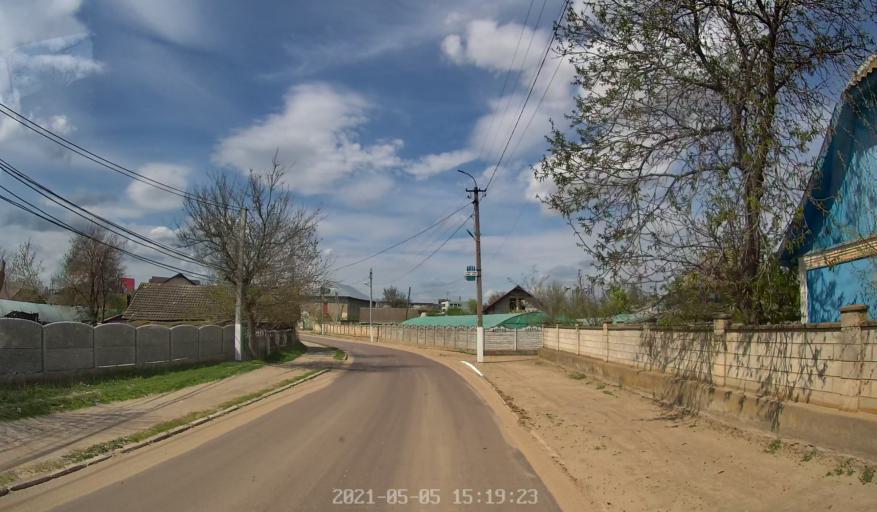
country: MD
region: Criuleni
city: Criuleni
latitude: 47.1265
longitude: 29.1941
